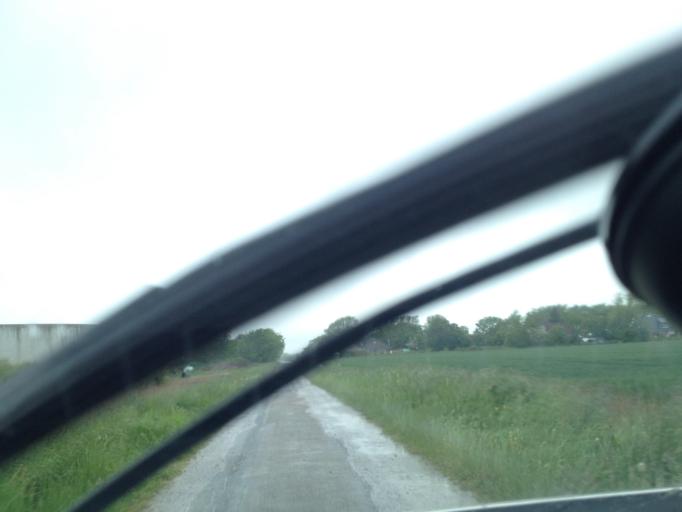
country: DE
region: Schleswig-Holstein
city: Klanxbull
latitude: 54.8857
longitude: 8.6912
